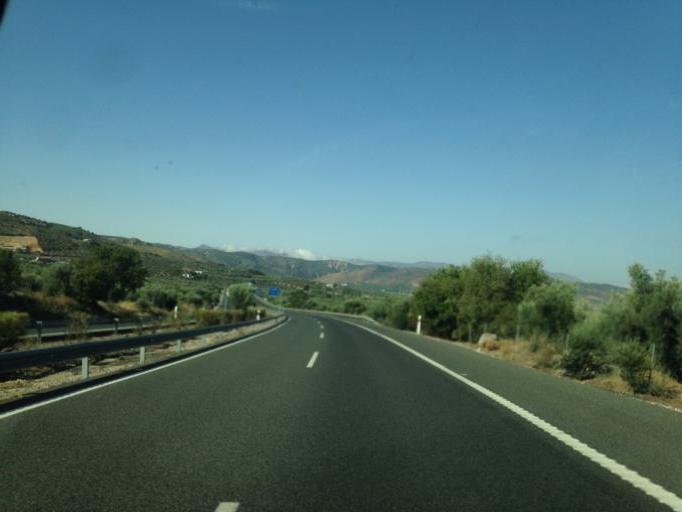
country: ES
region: Andalusia
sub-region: Provincia de Malaga
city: Archidona
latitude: 37.1034
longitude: -4.4041
